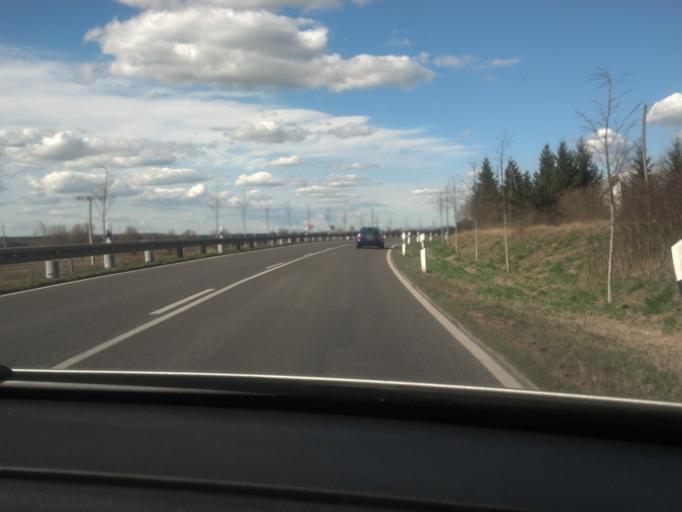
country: DE
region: Mecklenburg-Vorpommern
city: Trollenhagen
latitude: 53.6169
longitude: 13.2617
